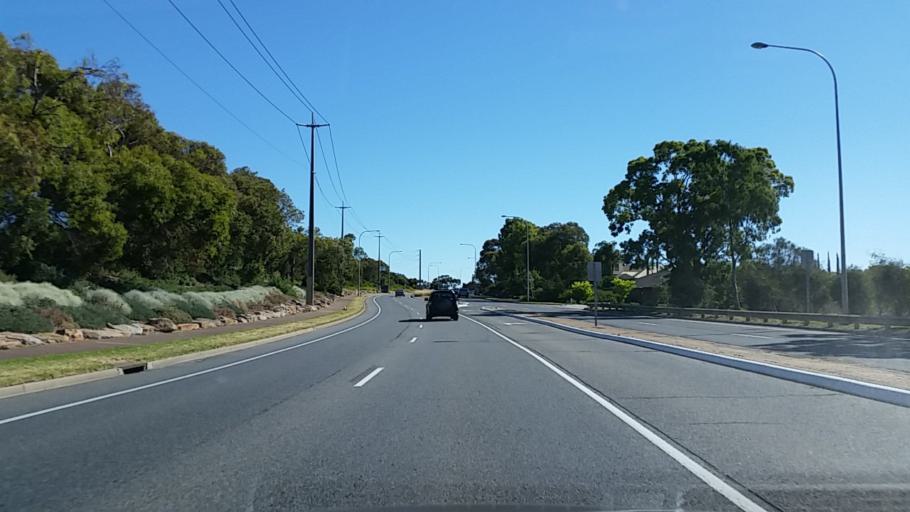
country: AU
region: South Australia
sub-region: Tea Tree Gully
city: Modbury
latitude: -34.8089
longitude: 138.6768
